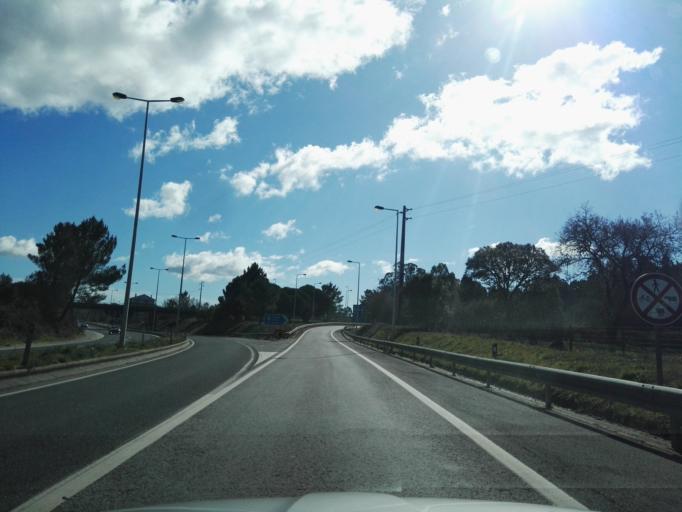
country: PT
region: Santarem
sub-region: Ourem
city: Fatima
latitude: 39.6315
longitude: -8.6845
